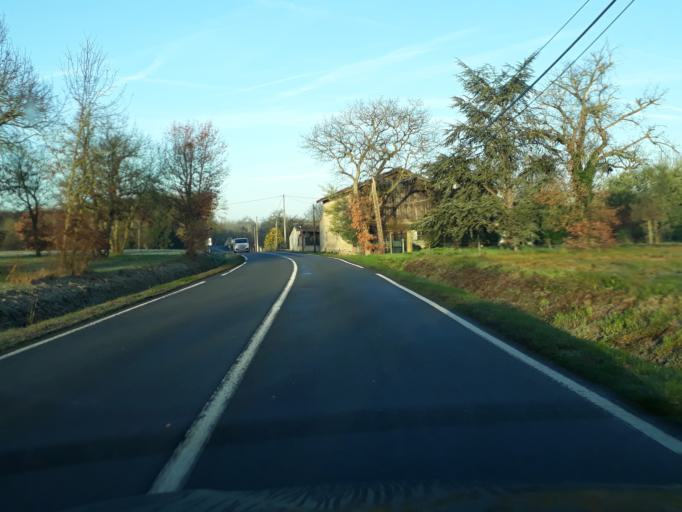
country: FR
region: Midi-Pyrenees
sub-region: Departement de la Haute-Garonne
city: Longages
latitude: 43.3575
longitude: 1.2193
